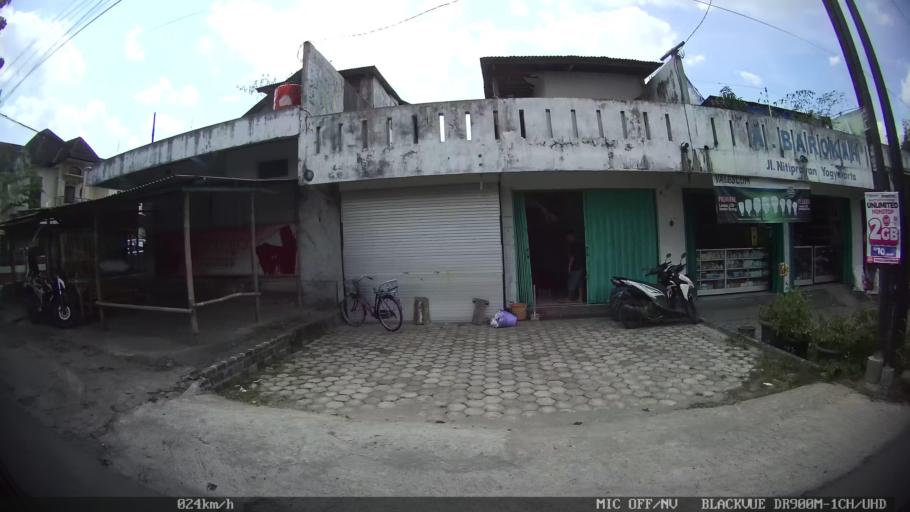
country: ID
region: Daerah Istimewa Yogyakarta
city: Kasihan
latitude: -7.8111
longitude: 110.3444
